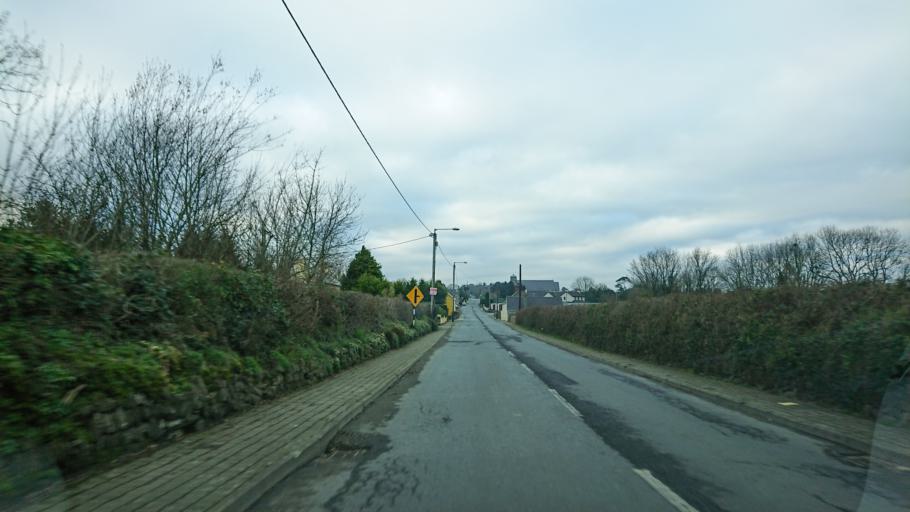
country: IE
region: Munster
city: Carrick-on-Suir
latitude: 52.3047
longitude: -7.4937
